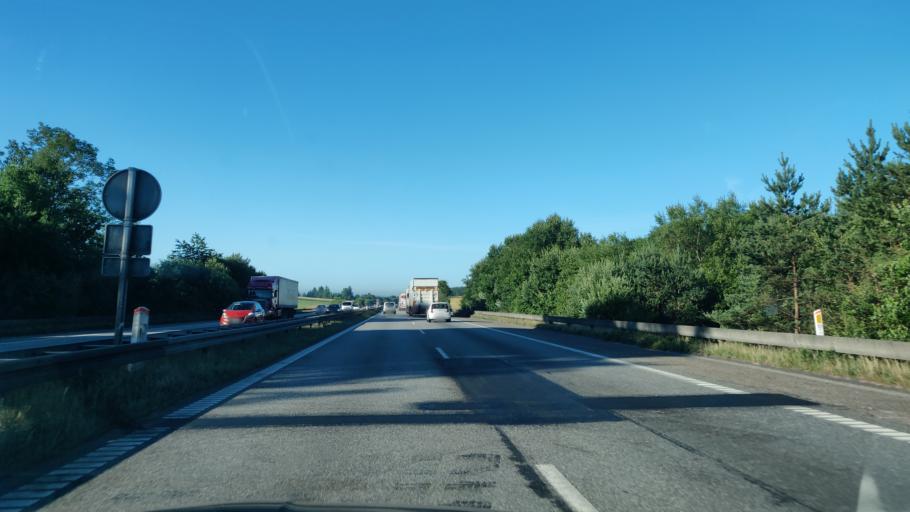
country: DK
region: North Denmark
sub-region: Rebild Kommune
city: Stovring
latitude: 56.9177
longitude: 9.8422
